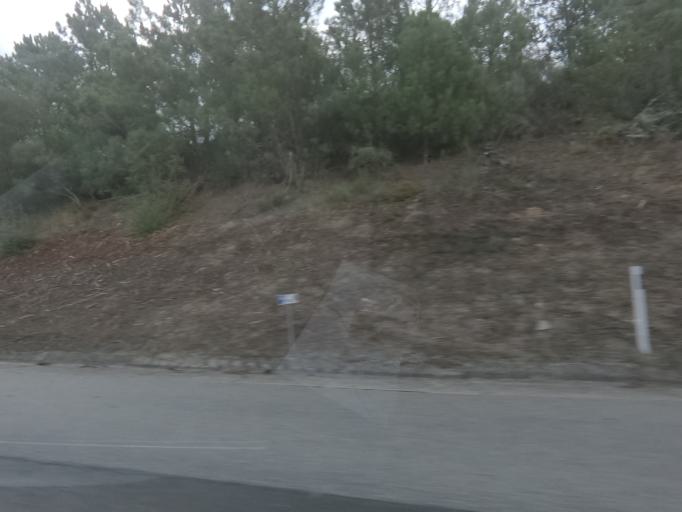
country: PT
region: Viseu
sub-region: Lamego
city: Lamego
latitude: 41.0538
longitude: -7.8404
